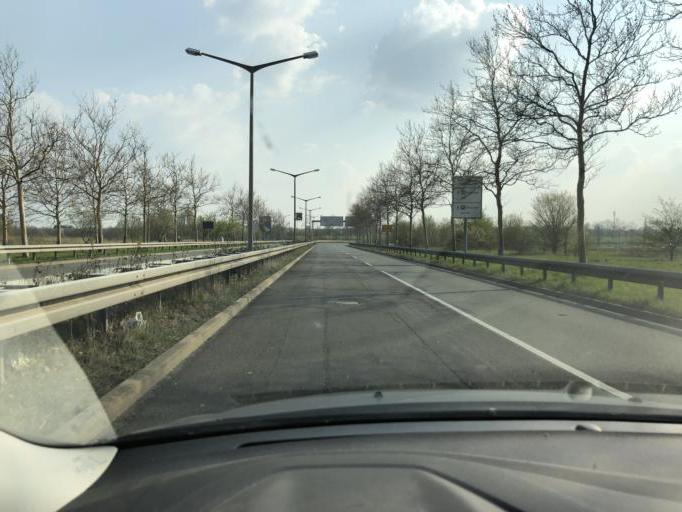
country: DE
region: Saxony
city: Rackwitz
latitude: 51.3946
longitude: 12.4209
